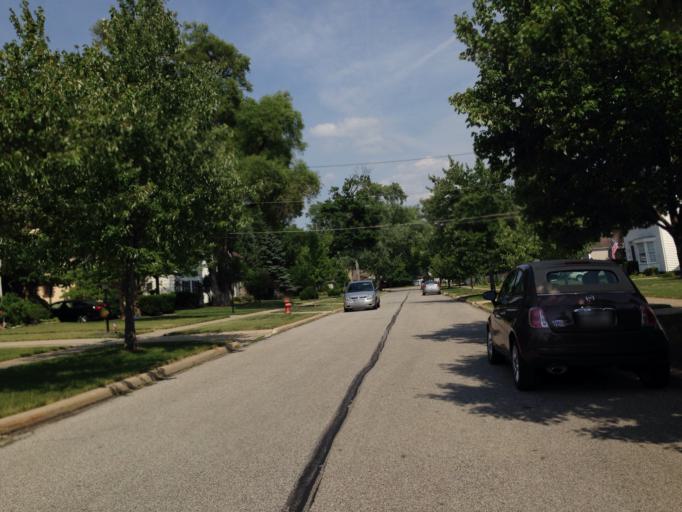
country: US
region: Ohio
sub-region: Cuyahoga County
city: Berea
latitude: 41.3687
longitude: -81.8601
